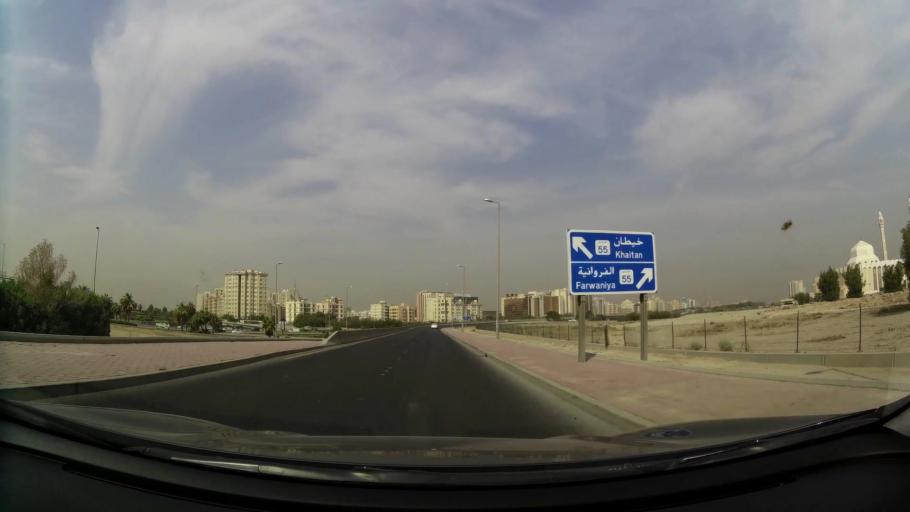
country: KW
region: Al Farwaniyah
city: Janub as Surrah
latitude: 29.2666
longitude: 47.9723
